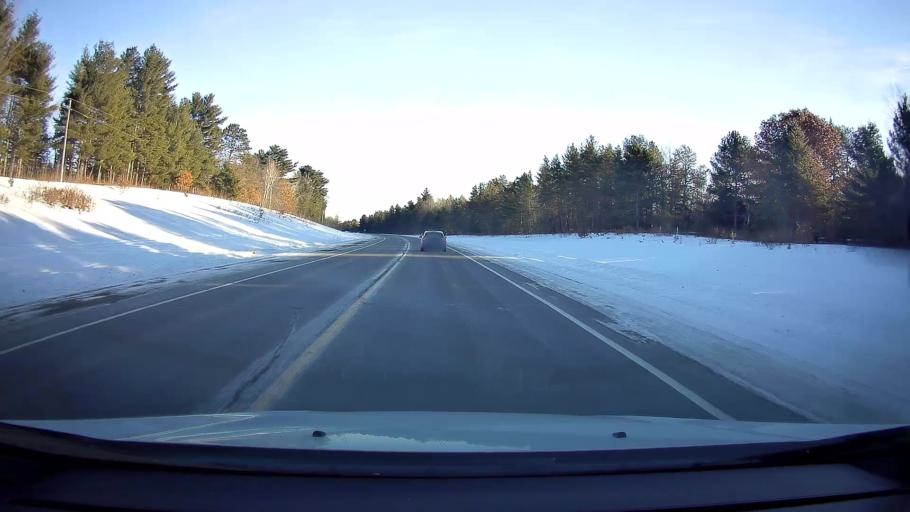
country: US
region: Wisconsin
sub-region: Washburn County
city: Spooner
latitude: 45.9351
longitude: -91.7057
